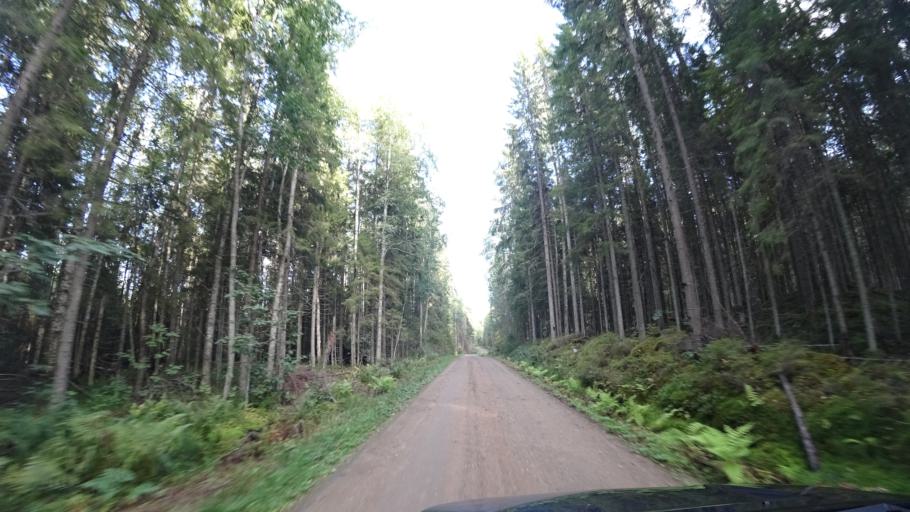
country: FI
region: Paijanne Tavastia
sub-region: Lahti
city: Auttoinen
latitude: 61.2201
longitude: 25.2044
